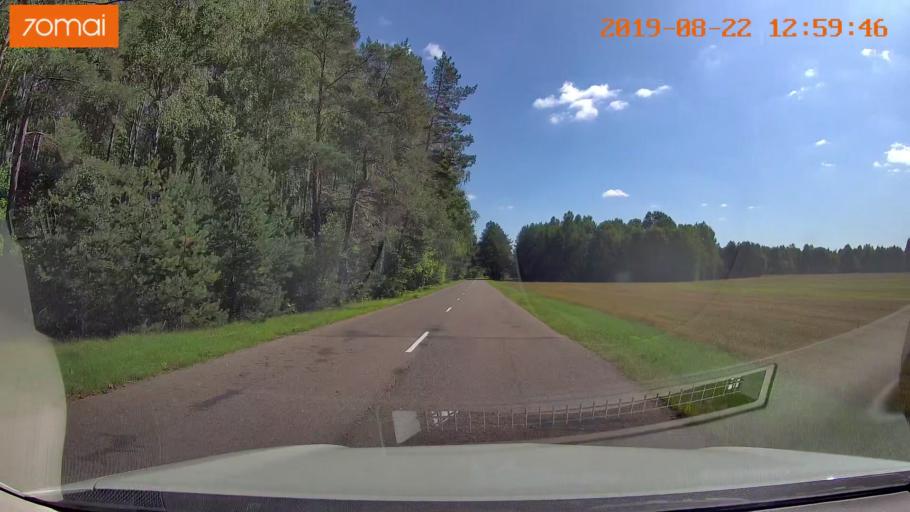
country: BY
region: Minsk
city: Prawdzinski
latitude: 53.4218
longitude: 27.7978
